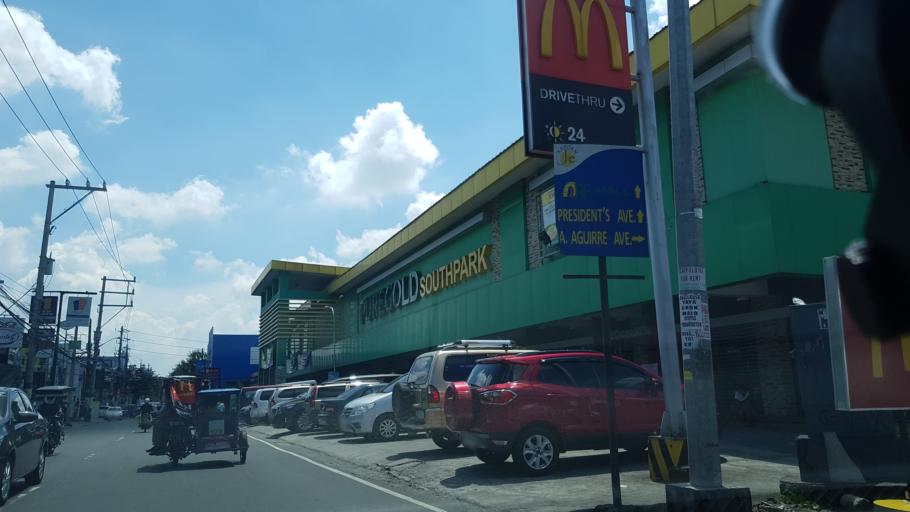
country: PH
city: Sambayanihan People's Village
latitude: 14.4476
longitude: 121.0292
